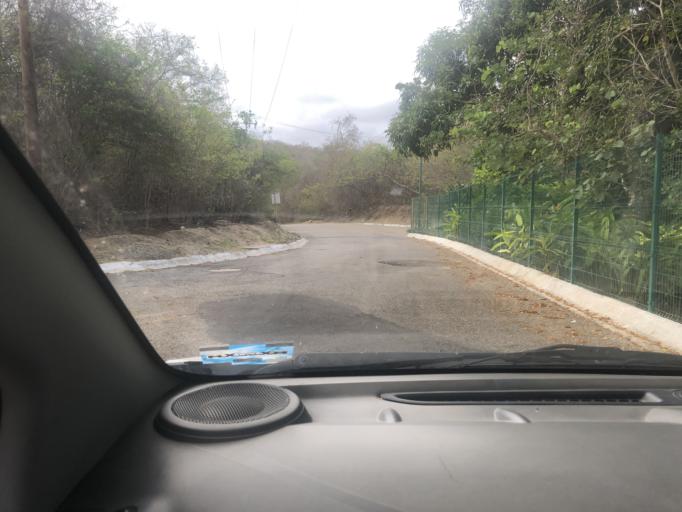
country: MX
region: Oaxaca
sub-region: Santa Maria Huatulco
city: Crucecita
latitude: 15.7737
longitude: -96.0868
